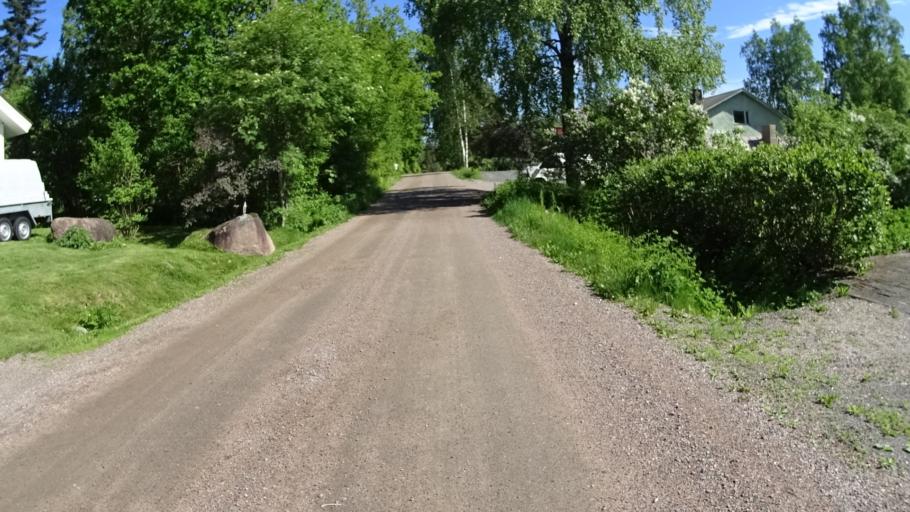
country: FI
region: Uusimaa
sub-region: Helsinki
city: Kilo
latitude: 60.2511
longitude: 24.7746
